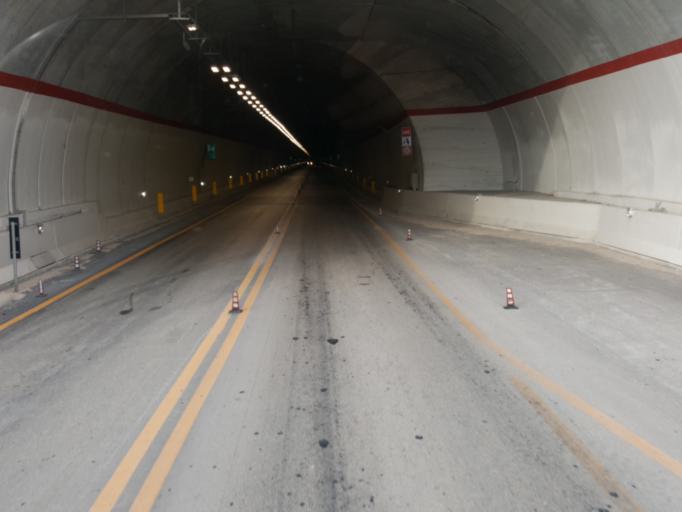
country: IT
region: Umbria
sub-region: Provincia di Perugia
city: Fossato di Vico
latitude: 43.3034
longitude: 12.8227
